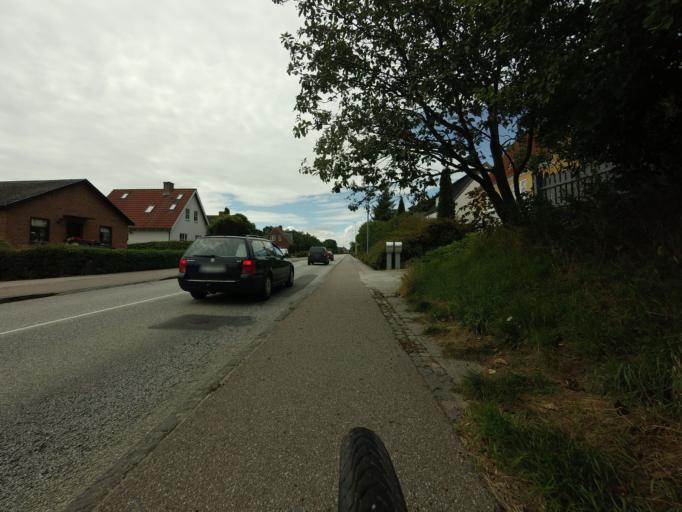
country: DK
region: Central Jutland
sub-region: Syddjurs Kommune
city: Ryomgard
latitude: 56.3798
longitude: 10.5120
